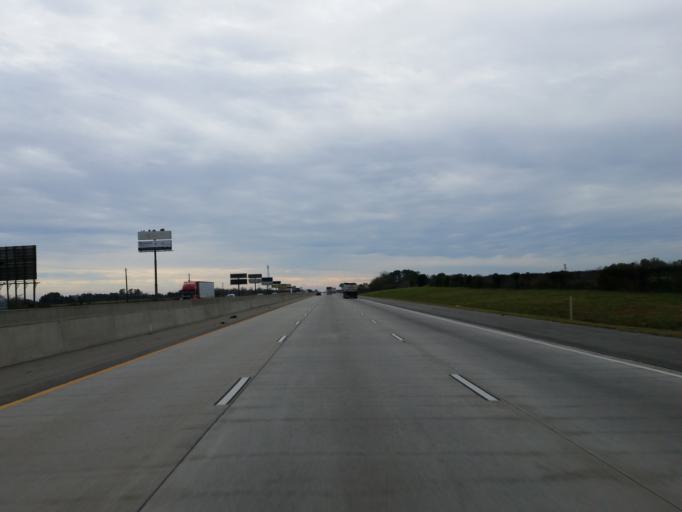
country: US
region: Georgia
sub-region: Tift County
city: Unionville
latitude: 31.3861
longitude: -83.4972
